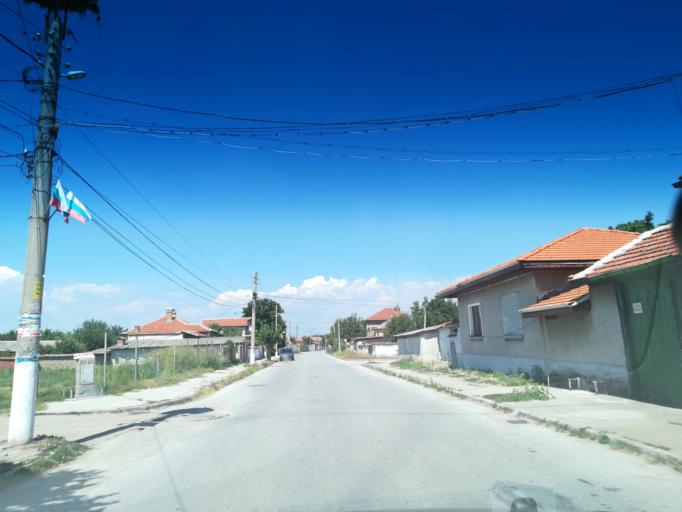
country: BG
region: Plovdiv
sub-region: Obshtina Sadovo
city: Sadovo
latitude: 42.0290
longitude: 25.1133
